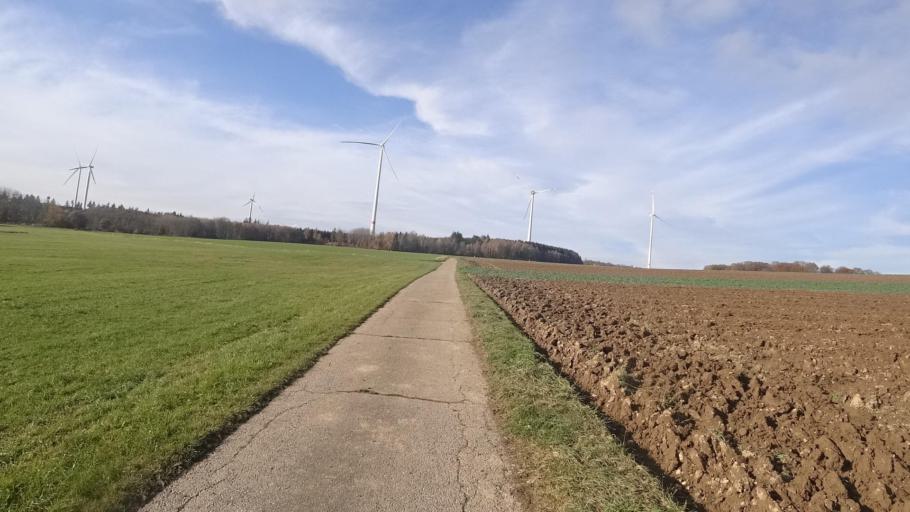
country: DE
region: Rheinland-Pfalz
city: Hausbay
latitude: 50.1058
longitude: 7.5519
